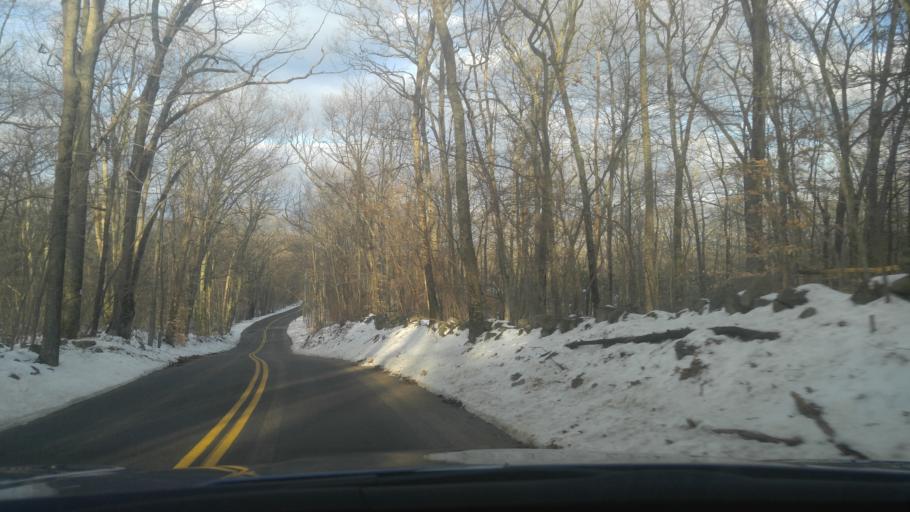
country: US
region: Rhode Island
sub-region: Kent County
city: Coventry
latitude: 41.7181
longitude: -71.6915
